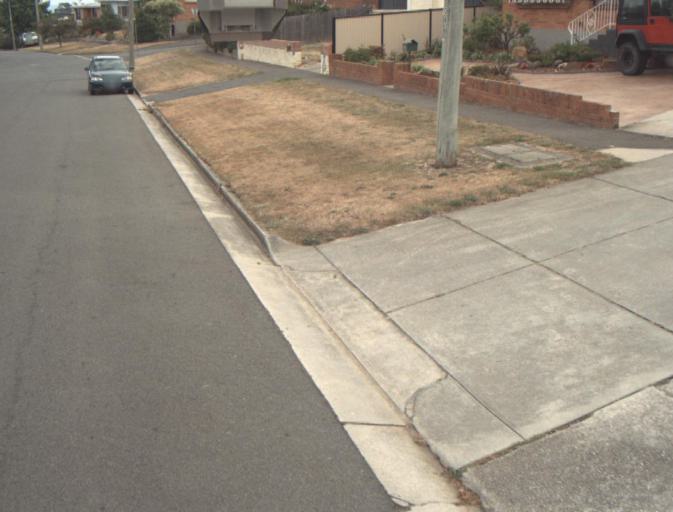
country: AU
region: Tasmania
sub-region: Launceston
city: Summerhill
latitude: -41.4794
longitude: 147.1690
